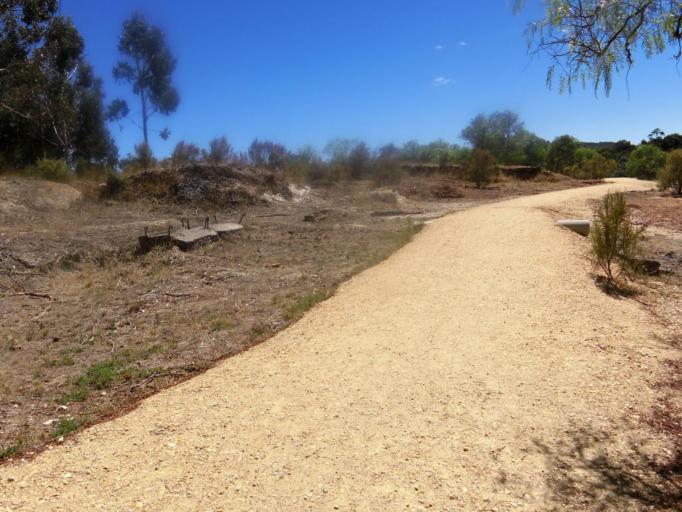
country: AU
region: Victoria
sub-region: Mount Alexander
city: Castlemaine
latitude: -36.9958
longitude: 144.0717
